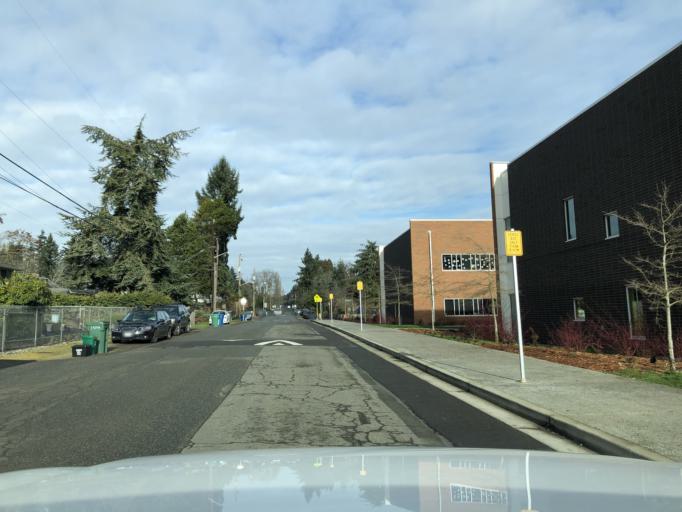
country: US
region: Washington
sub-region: King County
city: Lake Forest Park
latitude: 47.7240
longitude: -122.3073
